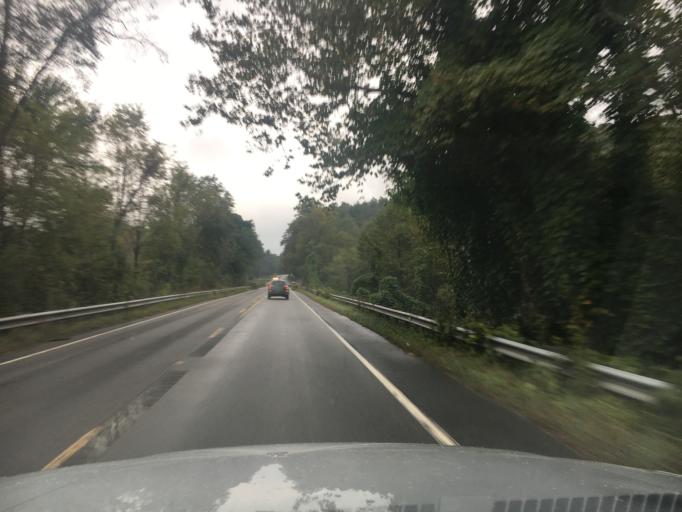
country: US
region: North Carolina
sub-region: Henderson County
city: Etowah
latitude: 35.3267
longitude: -82.5764
